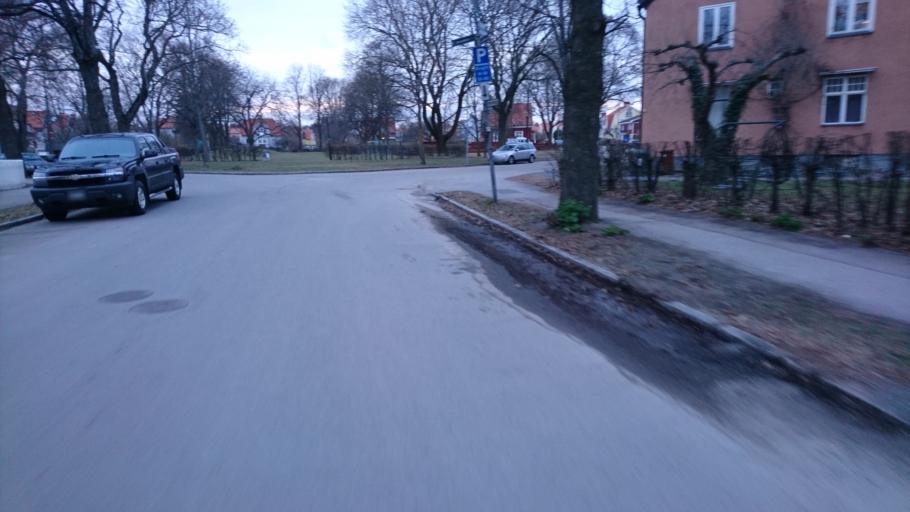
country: SE
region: Uppsala
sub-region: Uppsala Kommun
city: Uppsala
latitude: 59.8683
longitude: 17.6328
